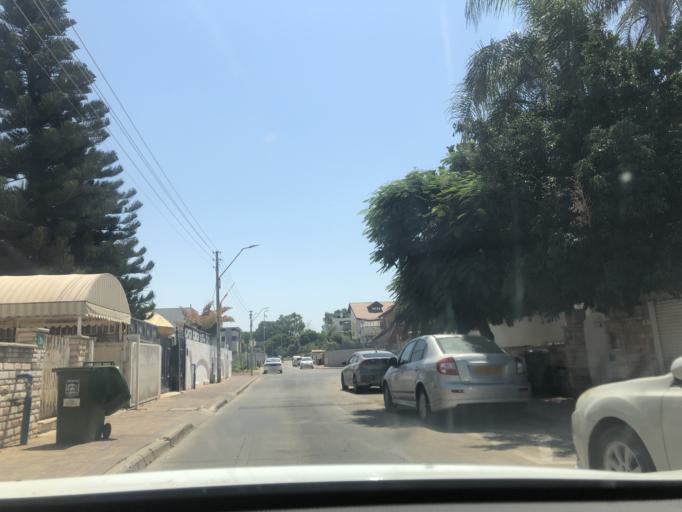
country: IL
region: Central District
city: Lod
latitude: 31.9378
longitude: 34.8894
